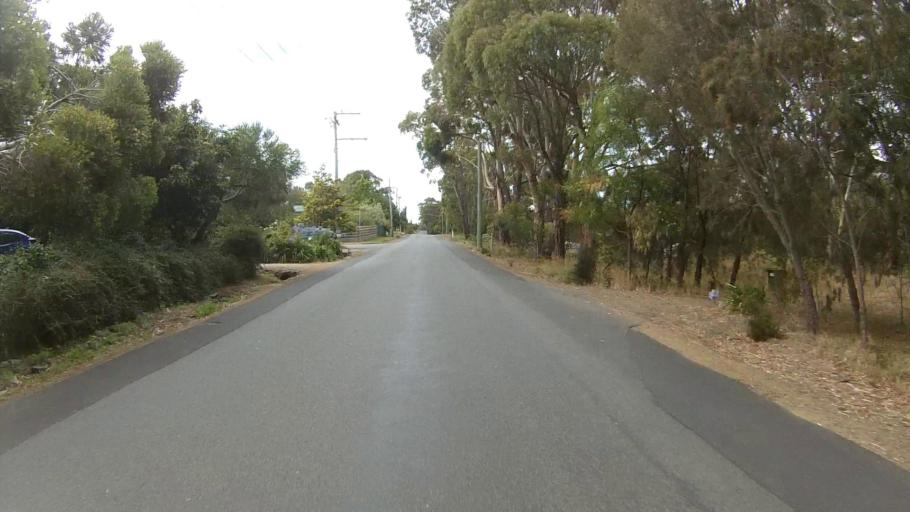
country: AU
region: Tasmania
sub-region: Kingborough
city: Margate
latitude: -43.0262
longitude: 147.2938
